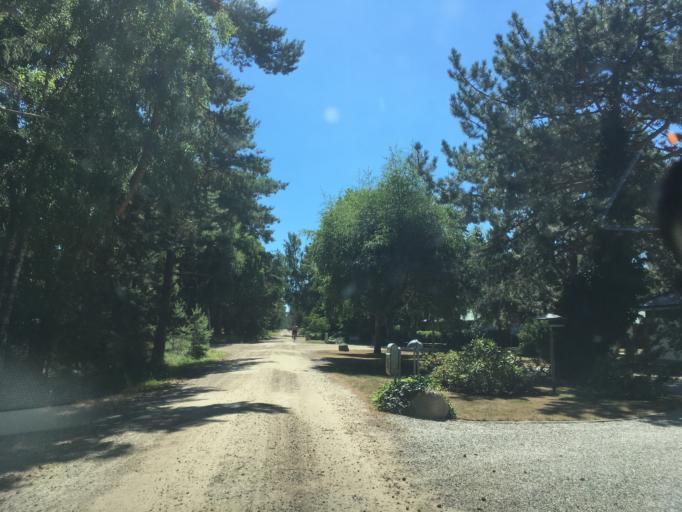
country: SE
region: Skane
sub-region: Vellinge Kommun
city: Ljunghusen
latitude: 55.4028
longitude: 12.9154
